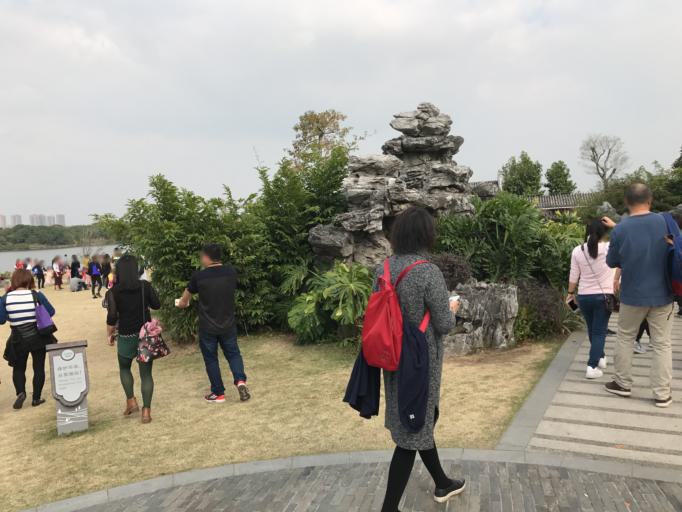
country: CN
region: Guangdong
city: Luopu
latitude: 23.0734
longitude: 113.3166
